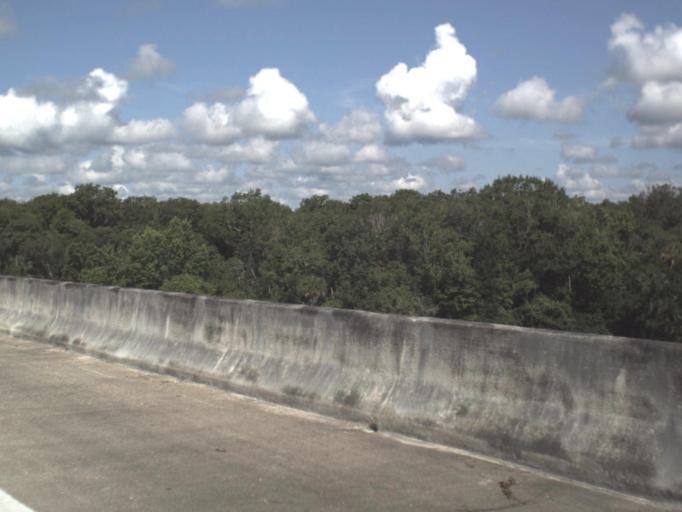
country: US
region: Florida
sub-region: Putnam County
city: Palatka
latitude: 29.5776
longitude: -81.6259
